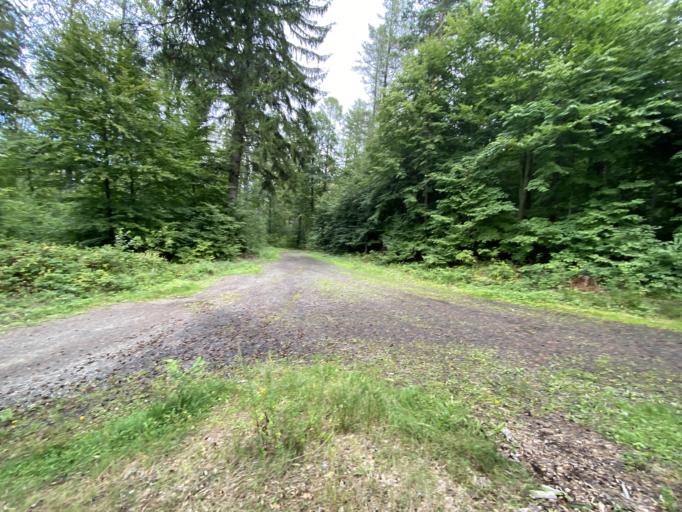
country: AT
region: Lower Austria
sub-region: Politischer Bezirk Wiener Neustadt
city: Wiesmath
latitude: 47.5706
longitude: 16.3295
